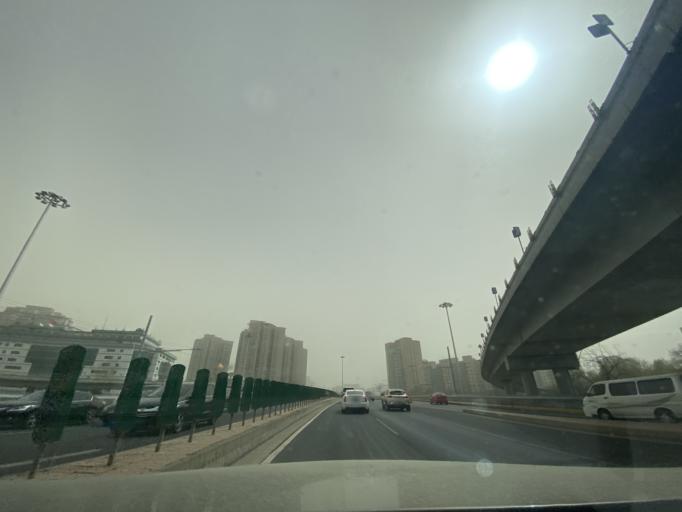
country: CN
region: Beijing
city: Sijiqing
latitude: 39.9414
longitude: 116.3028
